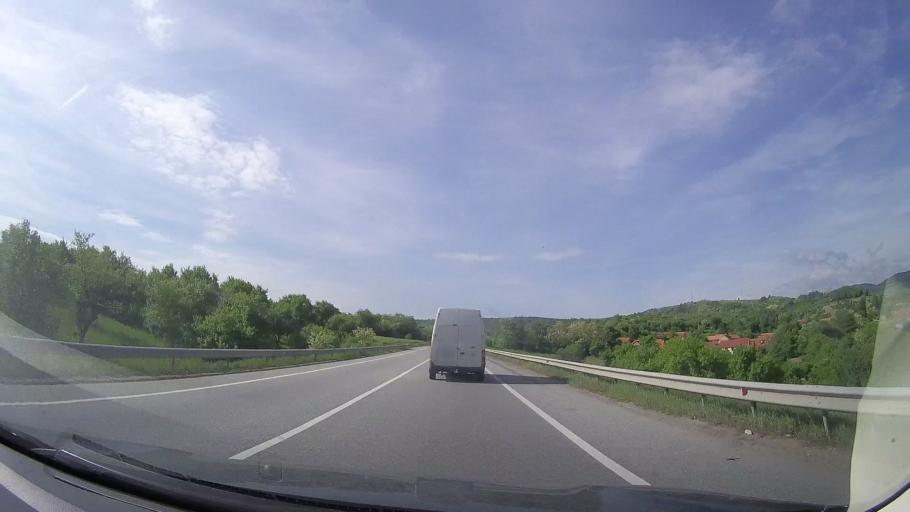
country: RO
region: Caras-Severin
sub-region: Comuna Domasnea
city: Domasnea
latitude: 45.0799
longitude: 22.3123
